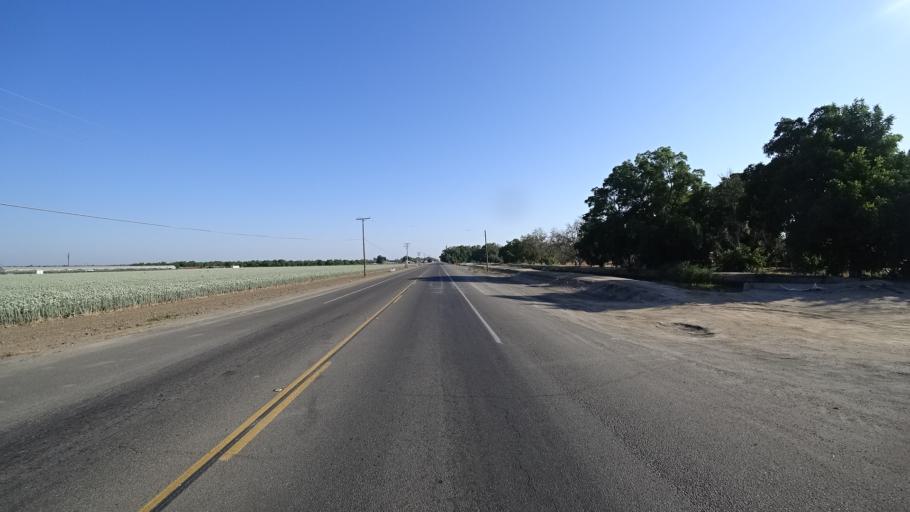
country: US
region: California
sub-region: Kings County
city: Armona
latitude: 36.3282
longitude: -119.7090
